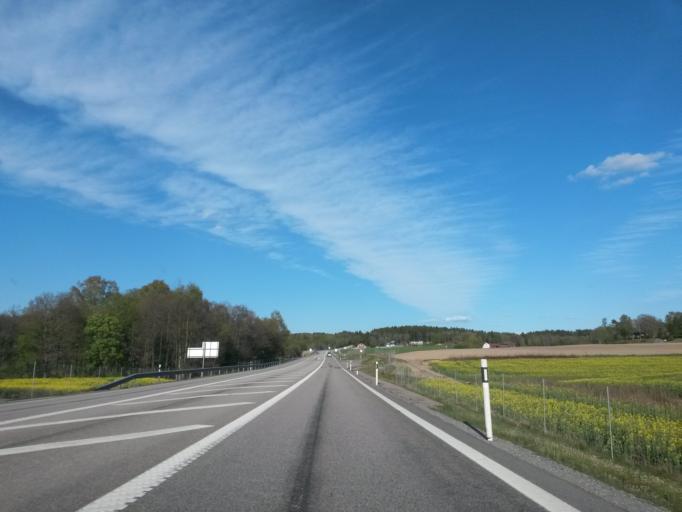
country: SE
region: Vaestra Goetaland
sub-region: Vargarda Kommun
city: Jonstorp
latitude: 58.0045
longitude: 12.7352
